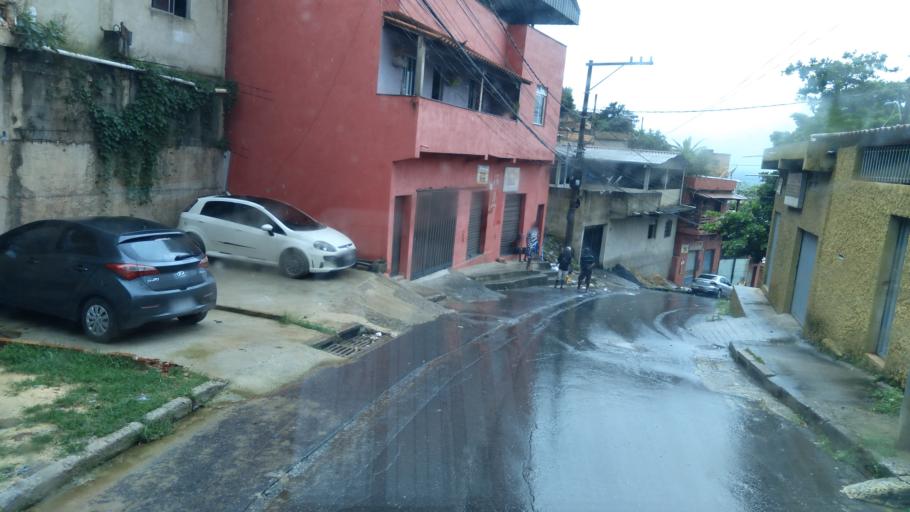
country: BR
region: Minas Gerais
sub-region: Belo Horizonte
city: Belo Horizonte
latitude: -19.9187
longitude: -43.8771
